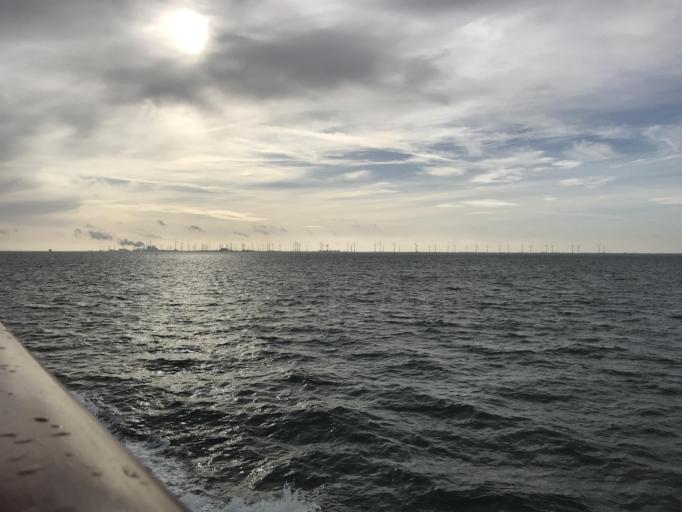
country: DE
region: Lower Saxony
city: Borkum
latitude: 53.5262
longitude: 6.7652
